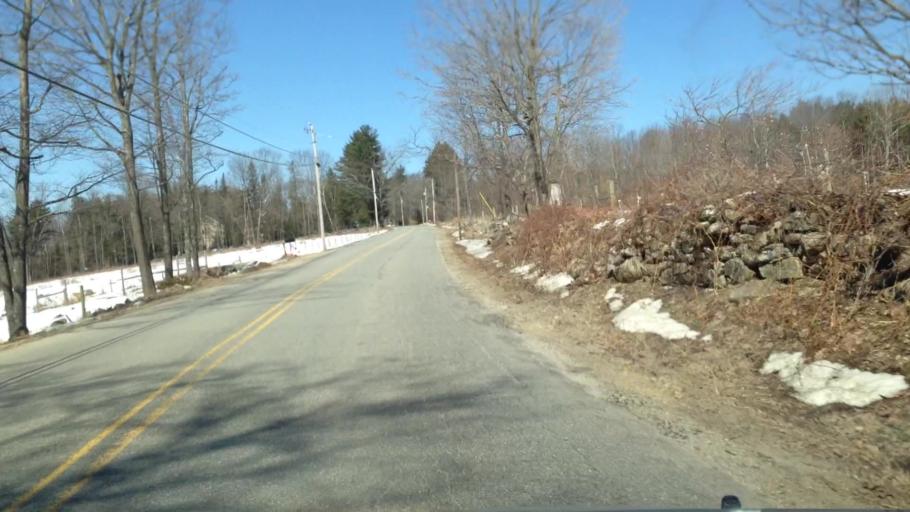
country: US
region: New Hampshire
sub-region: Hillsborough County
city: New Boston
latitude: 42.9864
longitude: -71.6480
